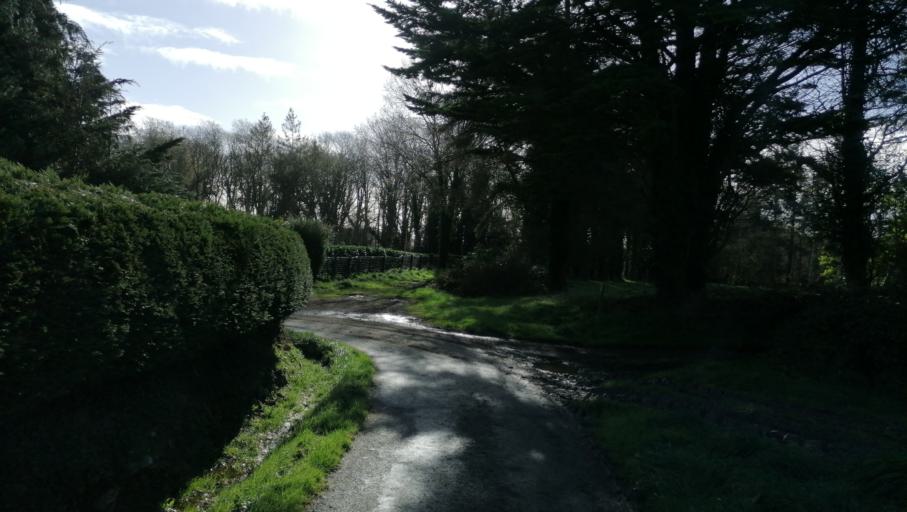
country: FR
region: Brittany
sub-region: Departement des Cotes-d'Armor
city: Pleguien
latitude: 48.6456
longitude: -2.9036
